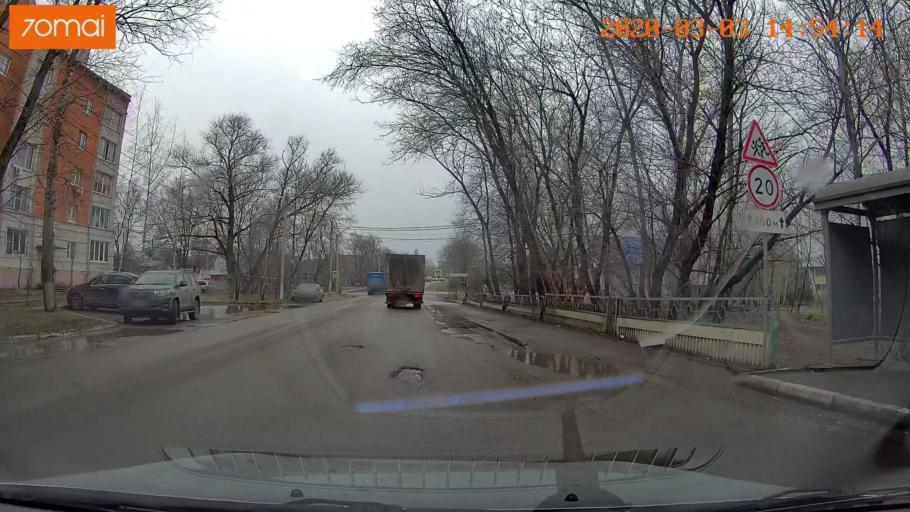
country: RU
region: Moskovskaya
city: Korenevo
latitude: 55.6712
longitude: 38.0031
